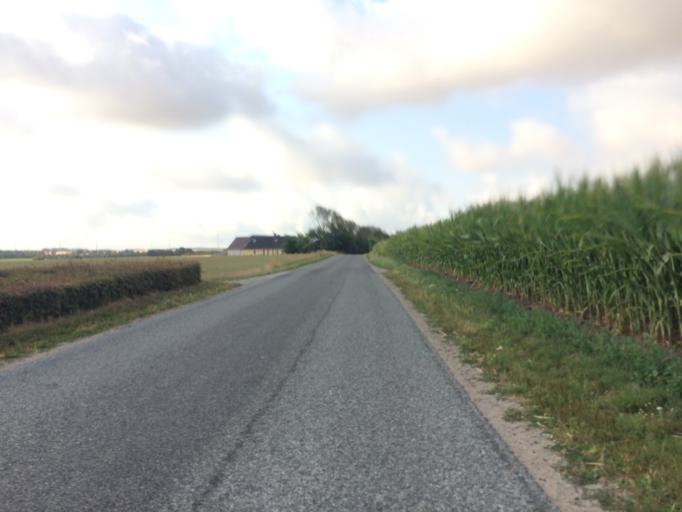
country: DK
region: Central Jutland
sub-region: Holstebro Kommune
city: Vinderup
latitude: 56.6160
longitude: 8.7618
